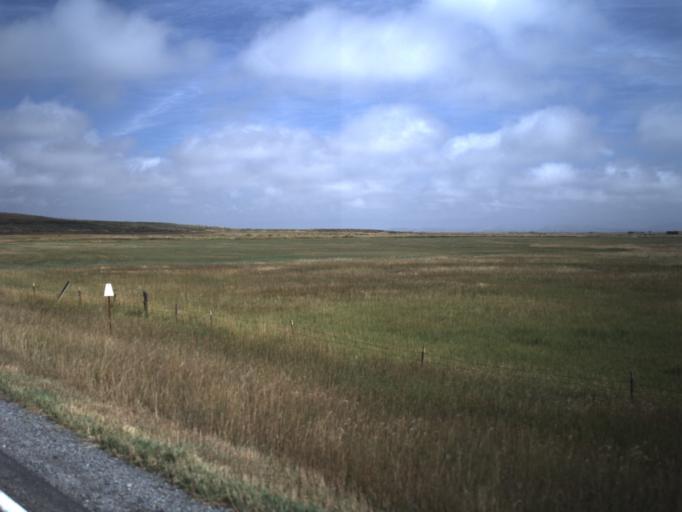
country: US
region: Utah
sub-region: Rich County
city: Randolph
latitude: 41.7222
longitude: -111.1592
